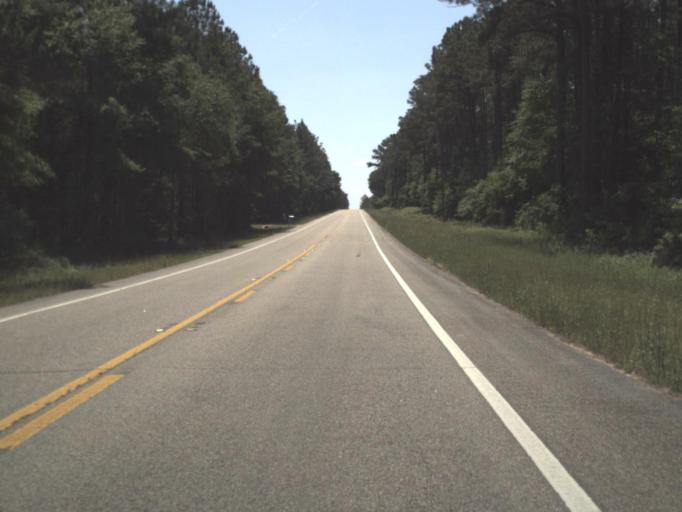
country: US
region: Florida
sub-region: Jackson County
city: Marianna
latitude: 30.6477
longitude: -85.2062
